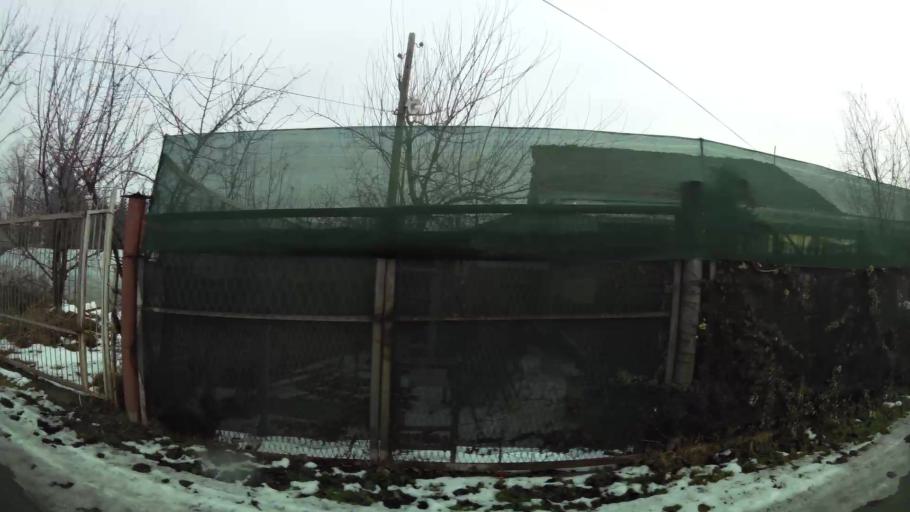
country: MK
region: Ilinden
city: Jurumleri
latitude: 41.9711
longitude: 21.5438
